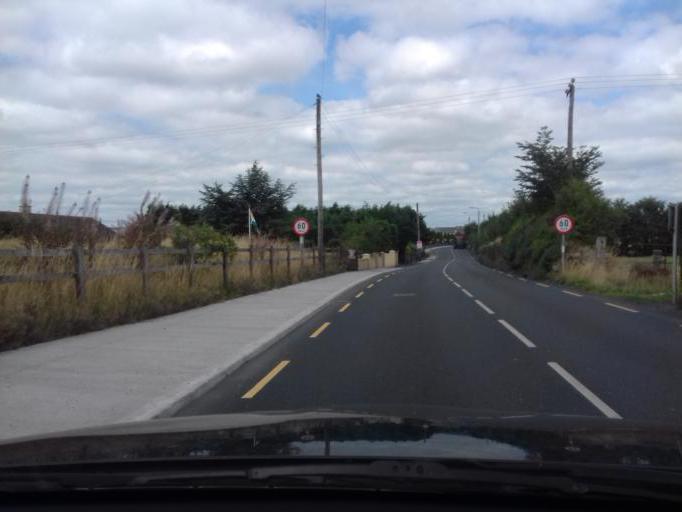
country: IE
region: Leinster
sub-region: County Carlow
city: Tullow
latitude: 52.7941
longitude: -6.7494
